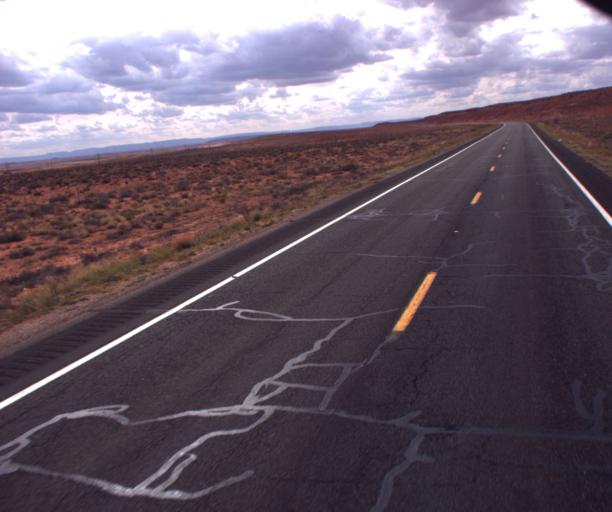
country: US
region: Arizona
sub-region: Navajo County
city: Kayenta
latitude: 36.9138
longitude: -109.7766
